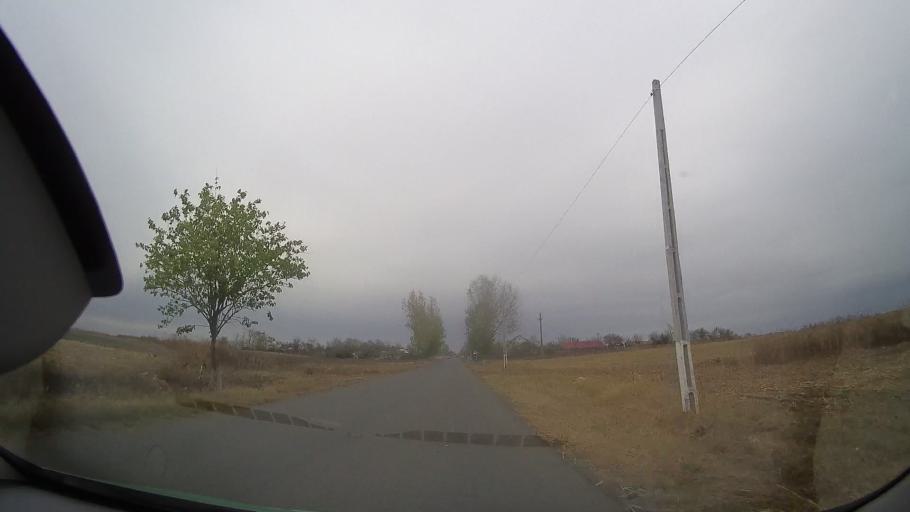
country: RO
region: Braila
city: Dudesti
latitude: 44.8726
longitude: 27.4294
